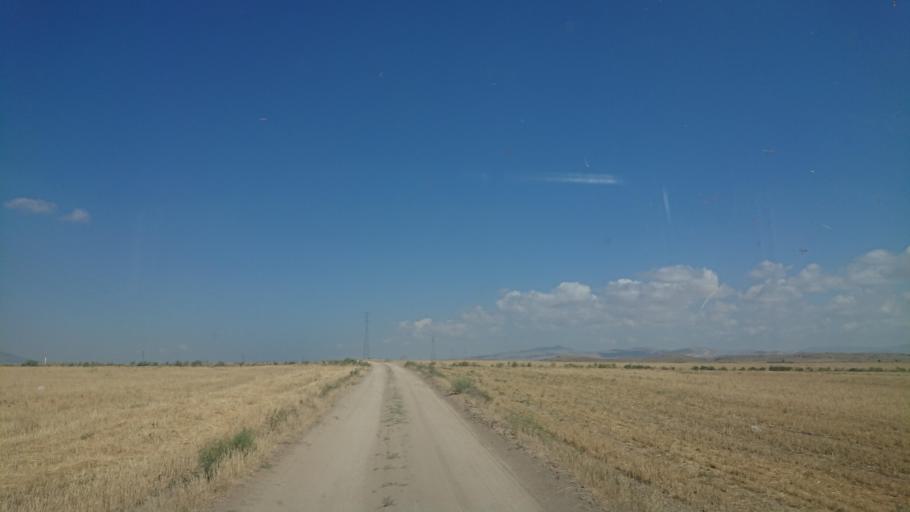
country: TR
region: Aksaray
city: Sariyahsi
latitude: 38.9993
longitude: 33.8923
